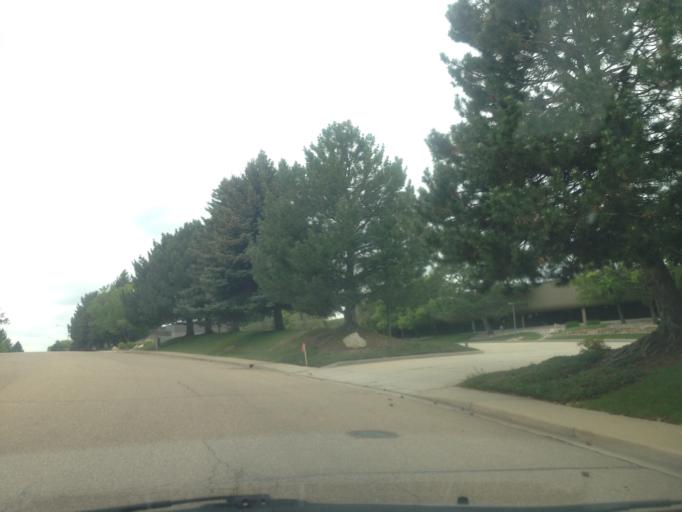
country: US
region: Colorado
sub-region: Boulder County
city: Longmont
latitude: 40.1431
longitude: -105.1247
